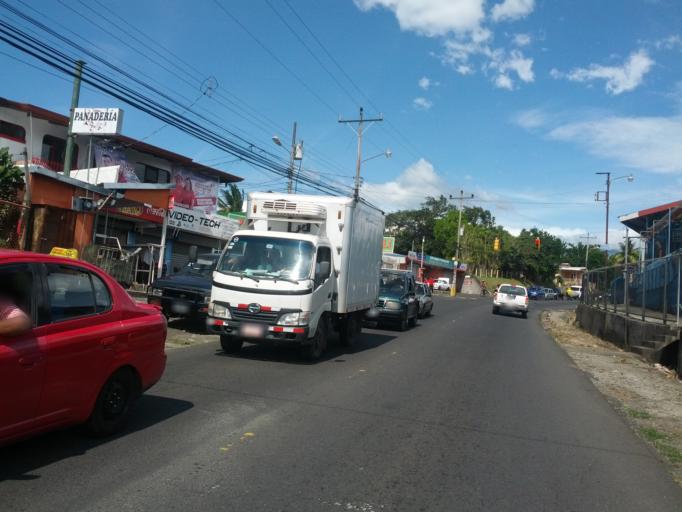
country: CR
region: Alajuela
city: Alajuela
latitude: 10.0223
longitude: -84.1892
